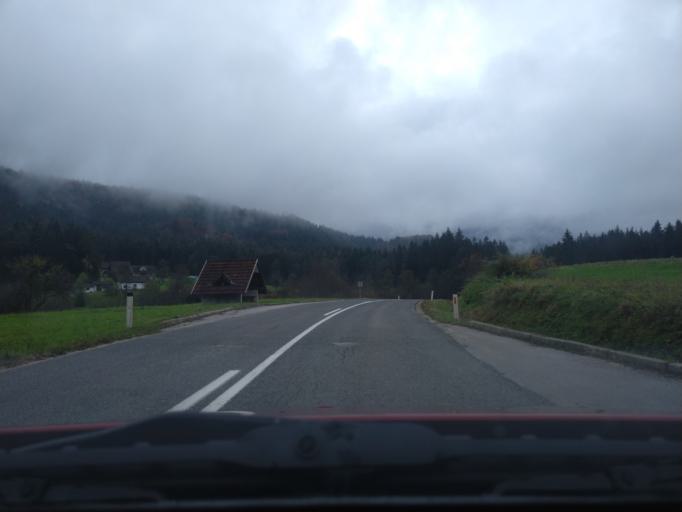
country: SI
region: Ljubno
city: Ljubno ob Savinji
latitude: 46.3184
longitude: 14.8494
